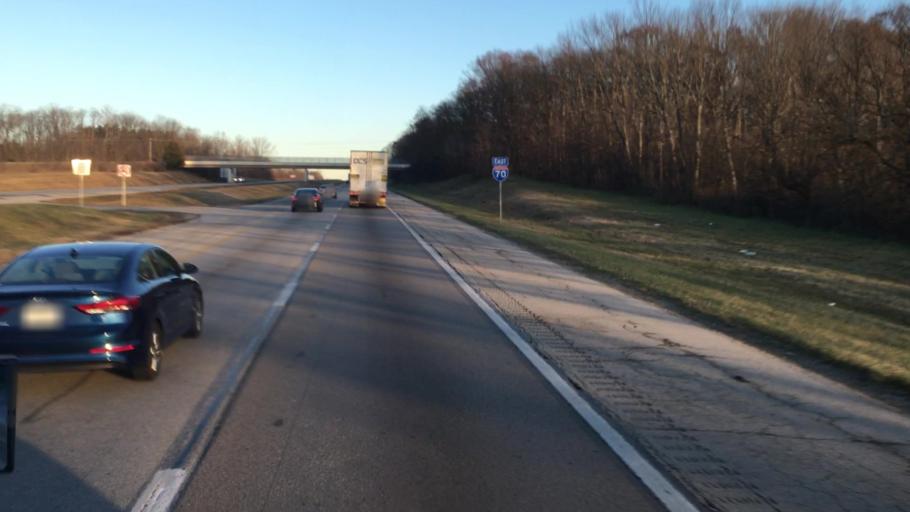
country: US
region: Ohio
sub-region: Preble County
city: Lewisburg
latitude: 39.8373
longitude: -84.5298
